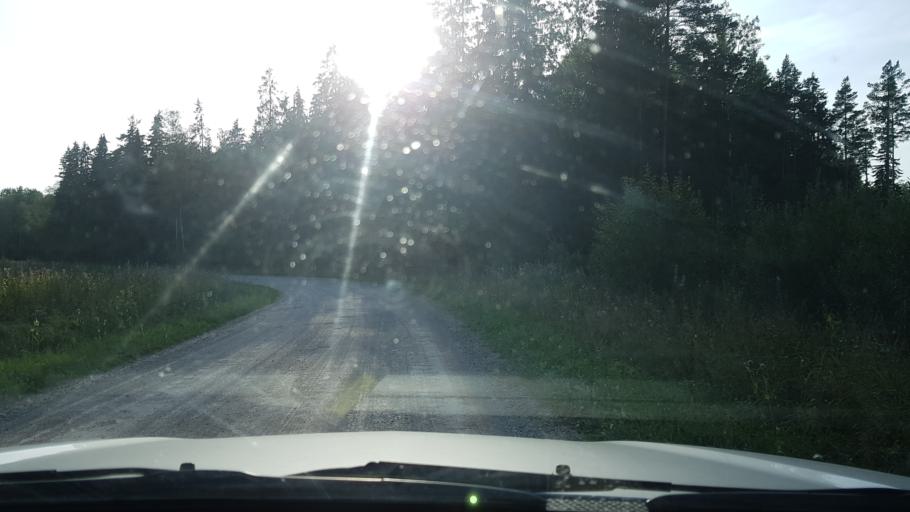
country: EE
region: Ida-Virumaa
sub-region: Narva-Joesuu linn
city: Narva-Joesuu
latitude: 59.3627
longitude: 28.0569
